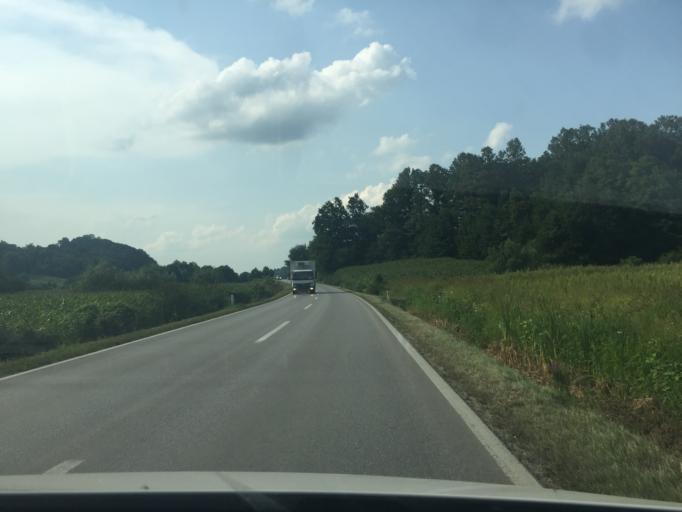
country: BA
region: Federation of Bosnia and Herzegovina
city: Mionica
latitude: 44.8116
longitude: 18.4742
